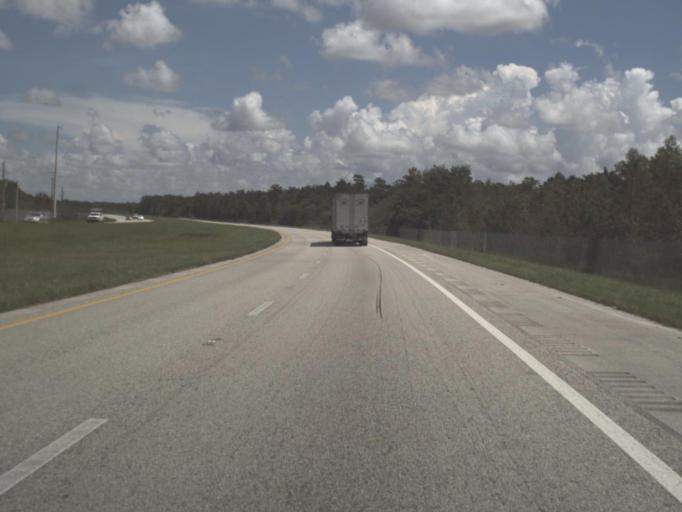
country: US
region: Florida
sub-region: Collier County
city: Immokalee
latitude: 26.1565
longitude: -81.2561
